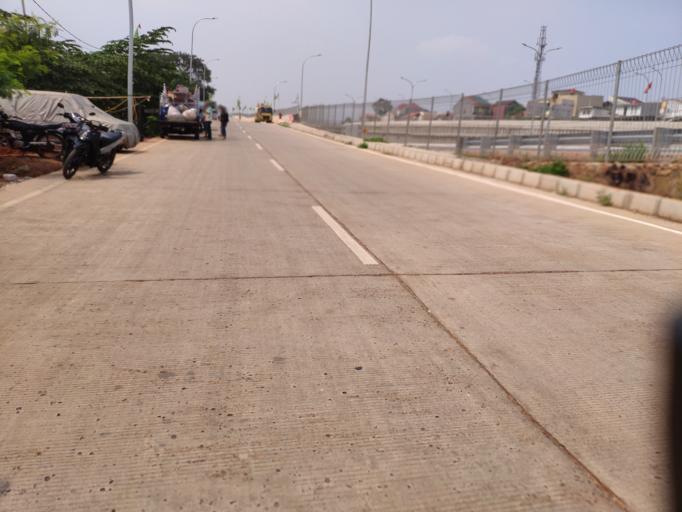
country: ID
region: West Java
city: Pamulang
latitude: -6.3294
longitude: 106.8009
